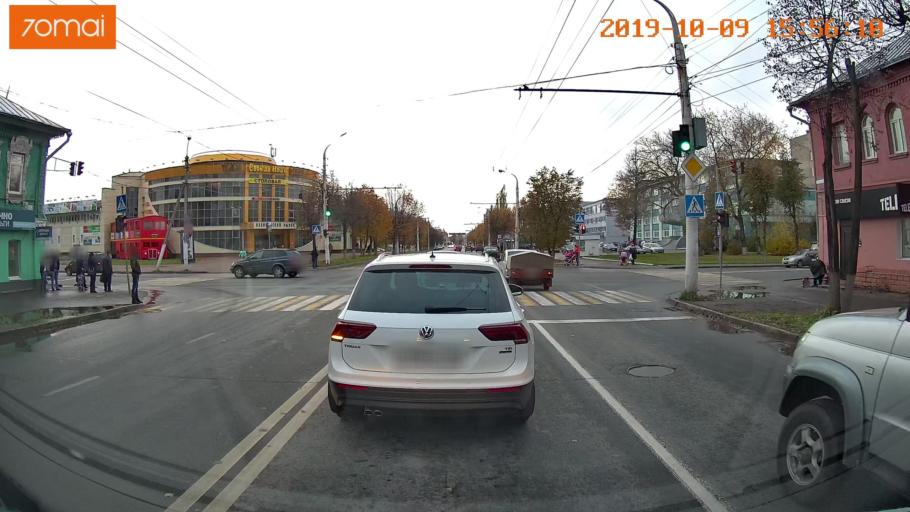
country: RU
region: Kostroma
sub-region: Kostromskoy Rayon
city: Kostroma
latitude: 57.7756
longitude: 40.9439
